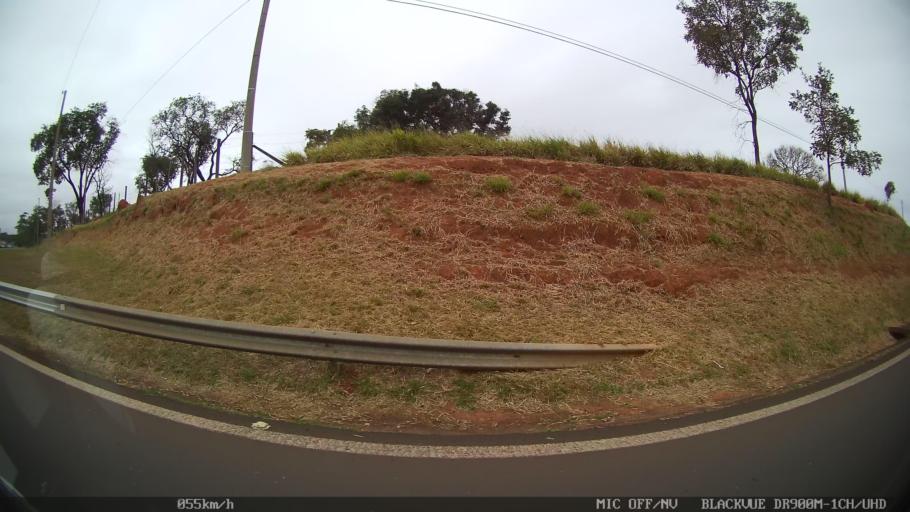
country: BR
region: Sao Paulo
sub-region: Sao Jose Do Rio Preto
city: Sao Jose do Rio Preto
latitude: -20.8200
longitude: -49.4333
